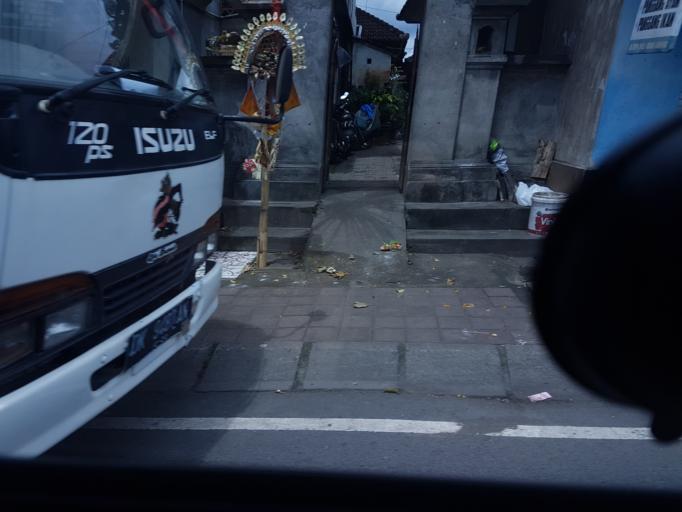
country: ID
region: Bali
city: Banjar Tebongkang
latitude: -8.5406
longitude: 115.2727
